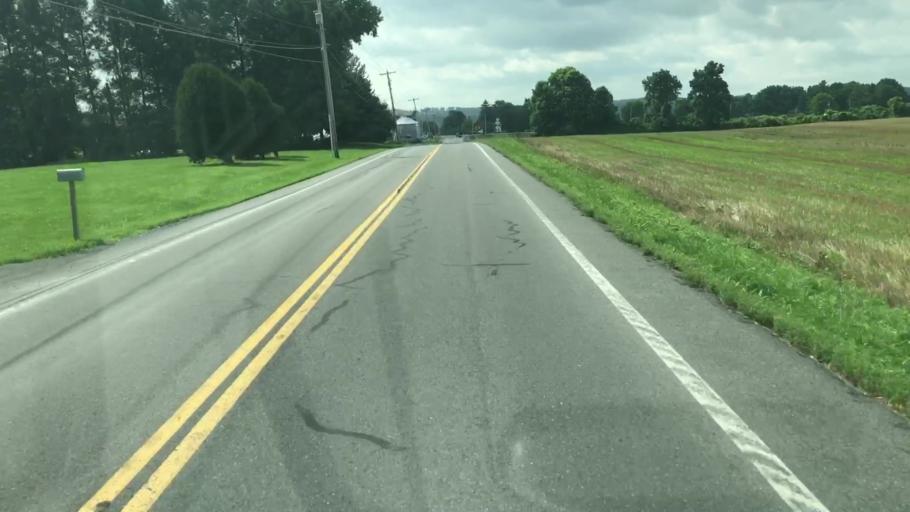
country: US
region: New York
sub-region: Onondaga County
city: Peru
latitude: 43.0388
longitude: -76.3657
